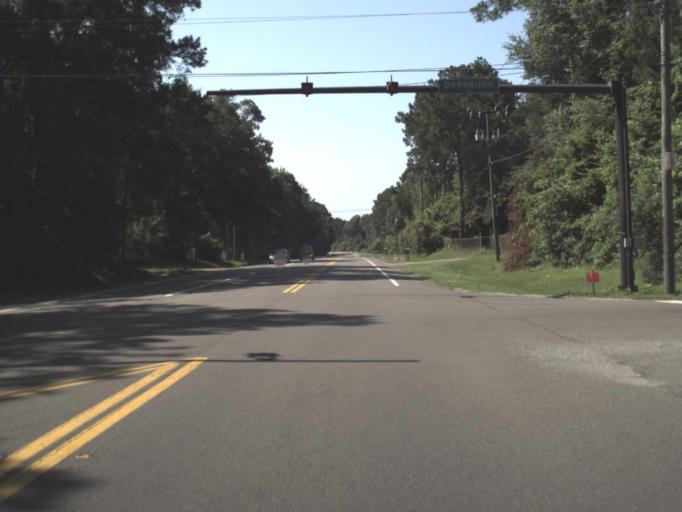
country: US
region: Florida
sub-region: Nassau County
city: Nassau Village-Ratliff
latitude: 30.5261
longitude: -81.7699
